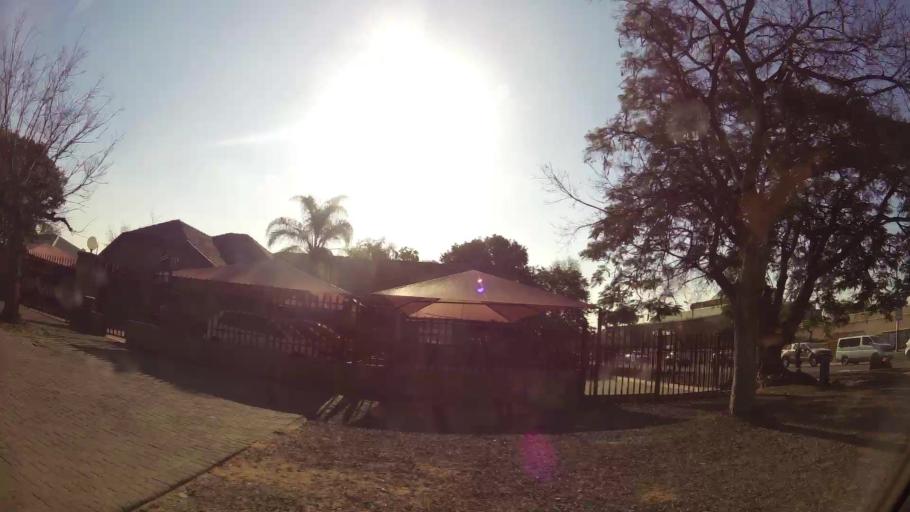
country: ZA
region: North-West
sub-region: Bojanala Platinum District Municipality
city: Rustenburg
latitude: -25.6758
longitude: 27.2419
